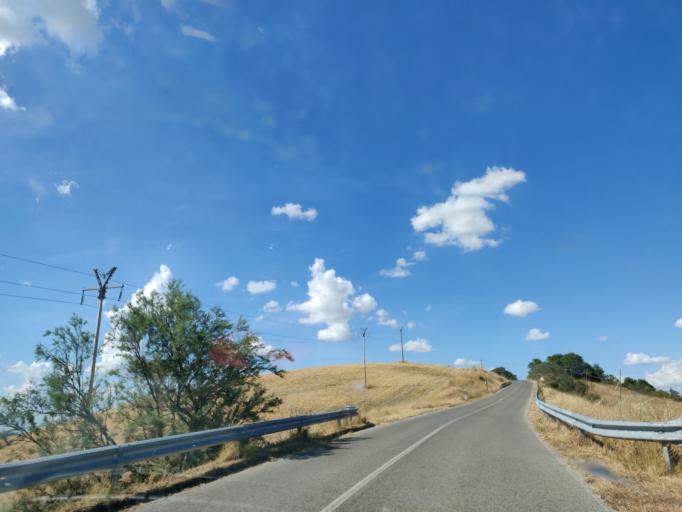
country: IT
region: Tuscany
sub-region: Provincia di Siena
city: Radicofani
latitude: 42.9322
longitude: 11.7321
